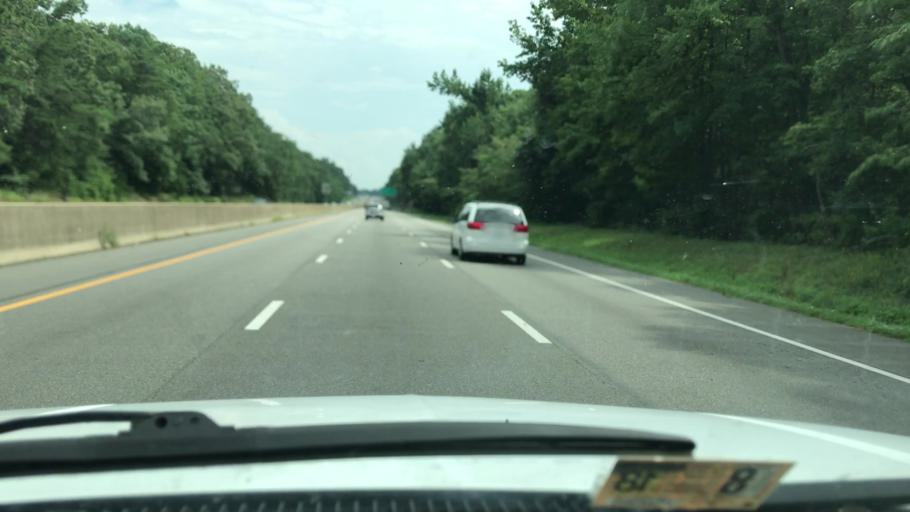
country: US
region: Virginia
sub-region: Chesterfield County
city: Bon Air
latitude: 37.4937
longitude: -77.5217
